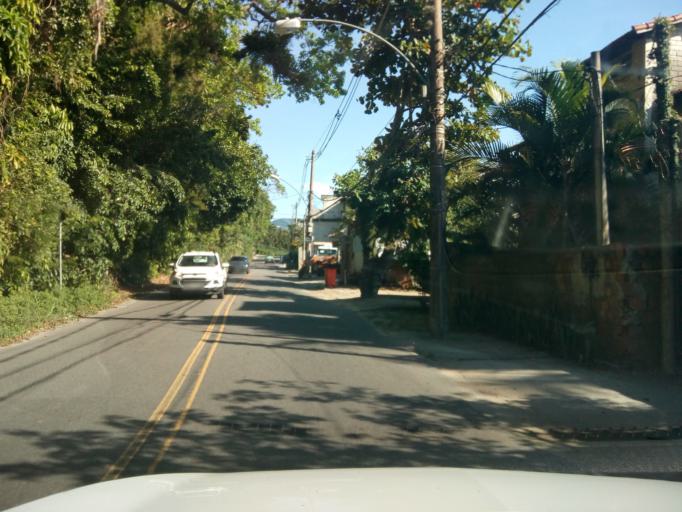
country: BR
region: Rio de Janeiro
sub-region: Nilopolis
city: Nilopolis
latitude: -23.0269
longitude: -43.5006
